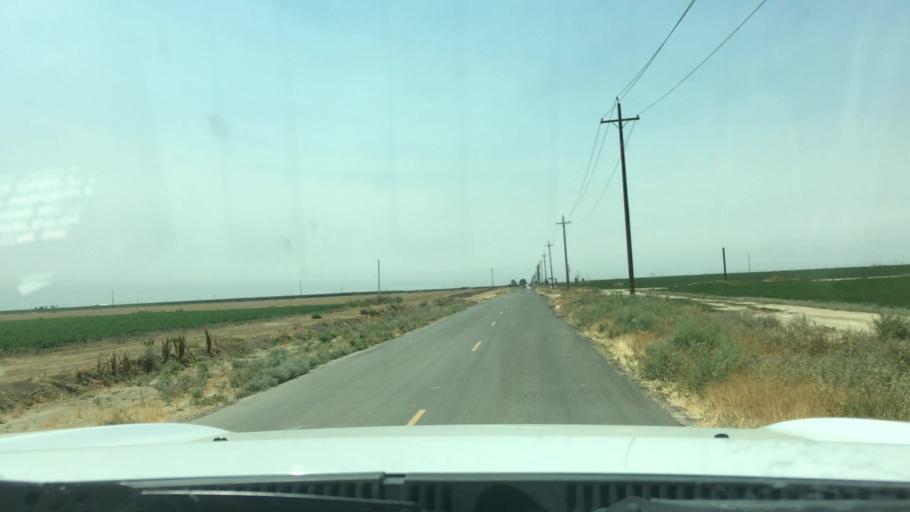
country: US
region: California
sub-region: Tulare County
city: Alpaugh
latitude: 35.7584
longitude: -119.4369
